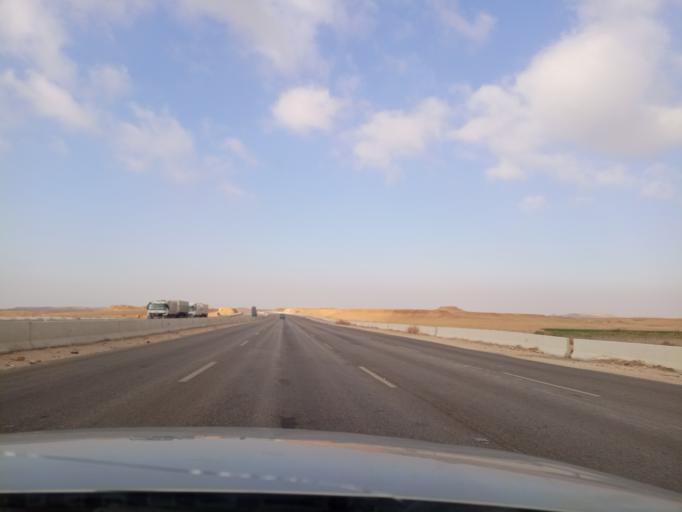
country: EG
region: Al Jizah
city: Al `Ayyat
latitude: 29.6707
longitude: 31.1921
